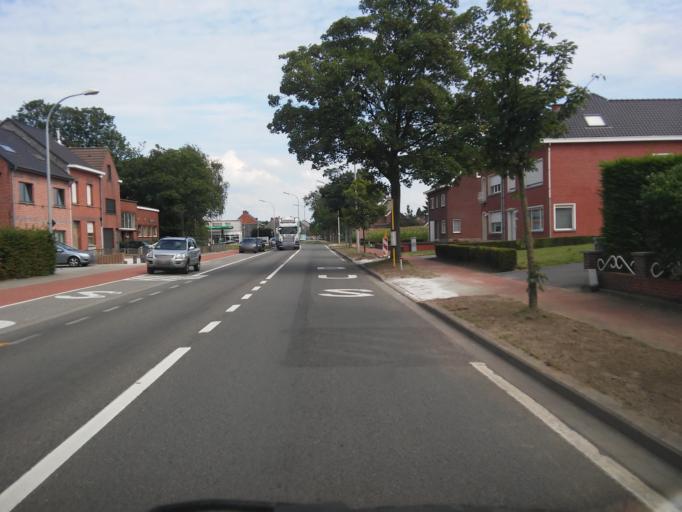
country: BE
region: Flanders
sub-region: Provincie Antwerpen
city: Willebroek
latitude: 51.0582
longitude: 4.3284
